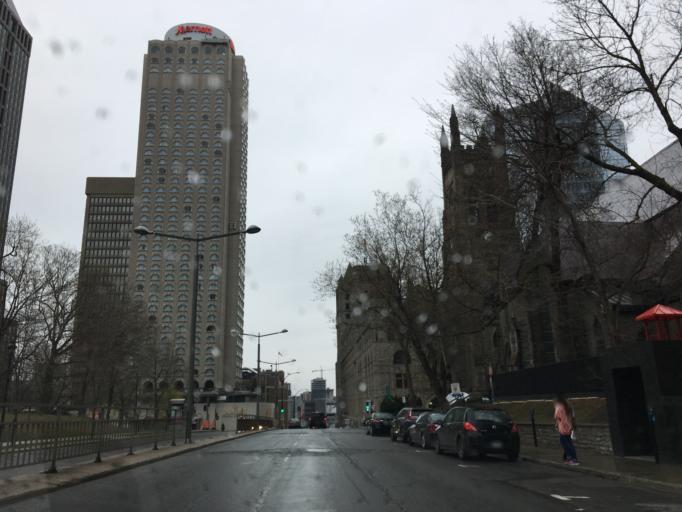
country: CA
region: Quebec
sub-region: Montreal
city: Montreal
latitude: 45.4982
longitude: -73.5697
